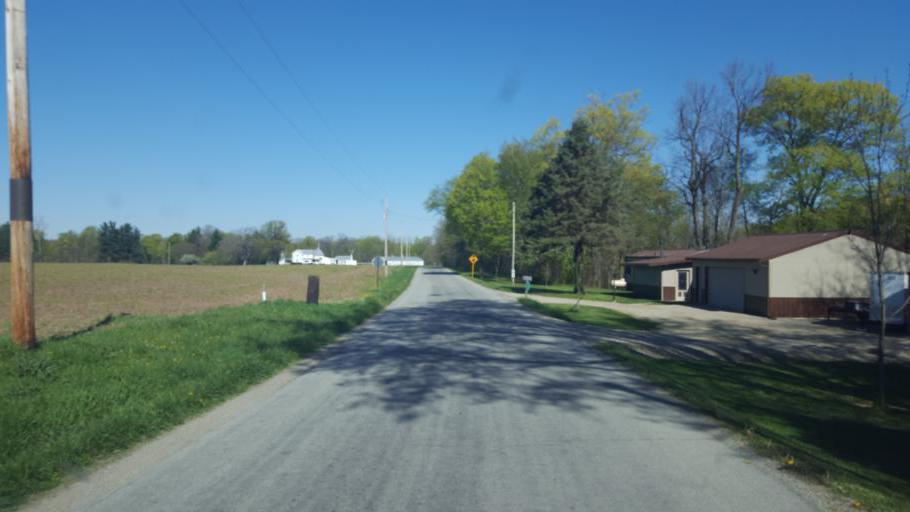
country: US
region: Ohio
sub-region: Wyandot County
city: Upper Sandusky
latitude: 40.9002
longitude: -83.2226
